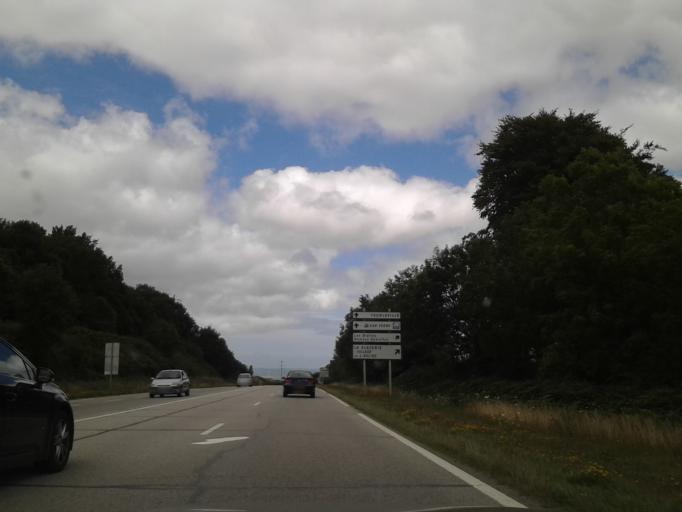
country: FR
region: Lower Normandy
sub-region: Departement de la Manche
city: La Glacerie
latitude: 49.6150
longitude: -1.5828
